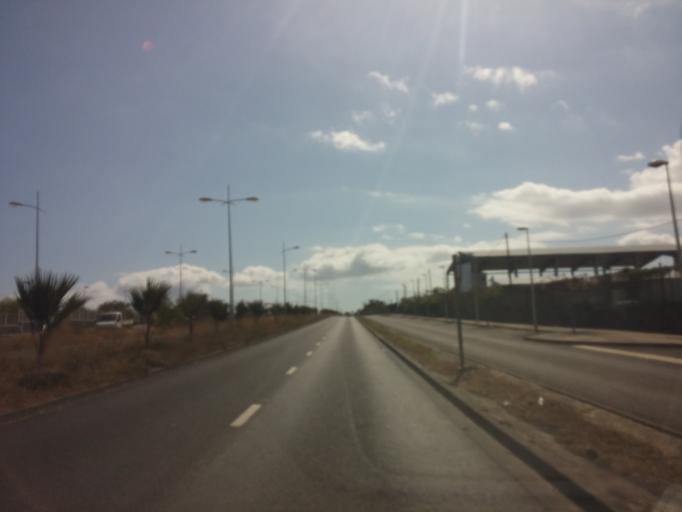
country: RE
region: Reunion
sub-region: Reunion
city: Le Port
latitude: -20.9696
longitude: 55.2959
